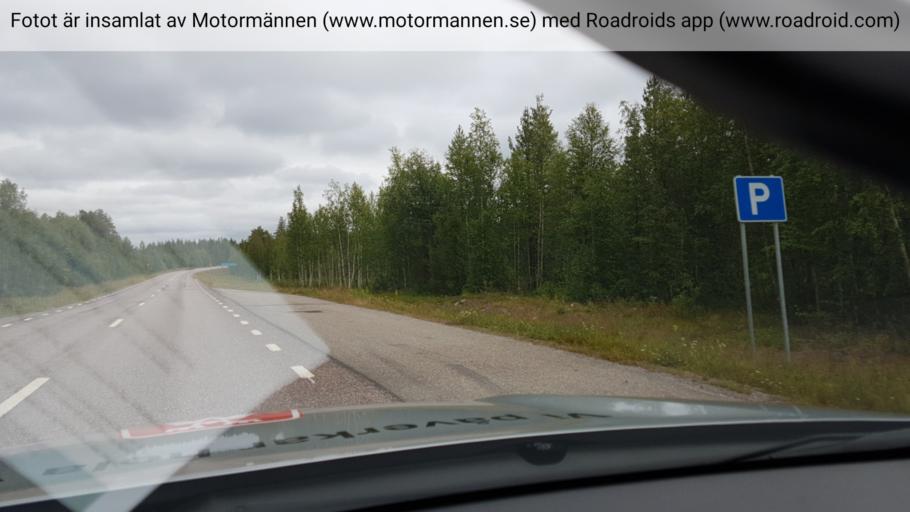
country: SE
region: Norrbotten
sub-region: Gallivare Kommun
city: Gaellivare
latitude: 67.0614
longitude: 21.2655
